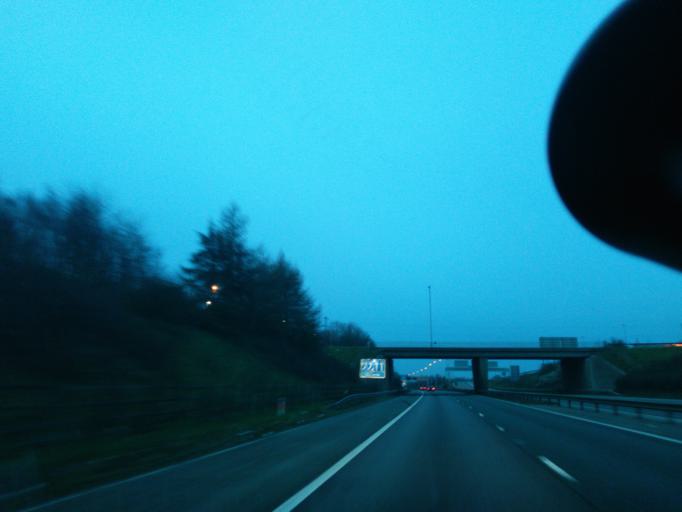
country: GB
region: England
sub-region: Warwickshire
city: Curdworth
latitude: 52.5384
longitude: -1.7264
